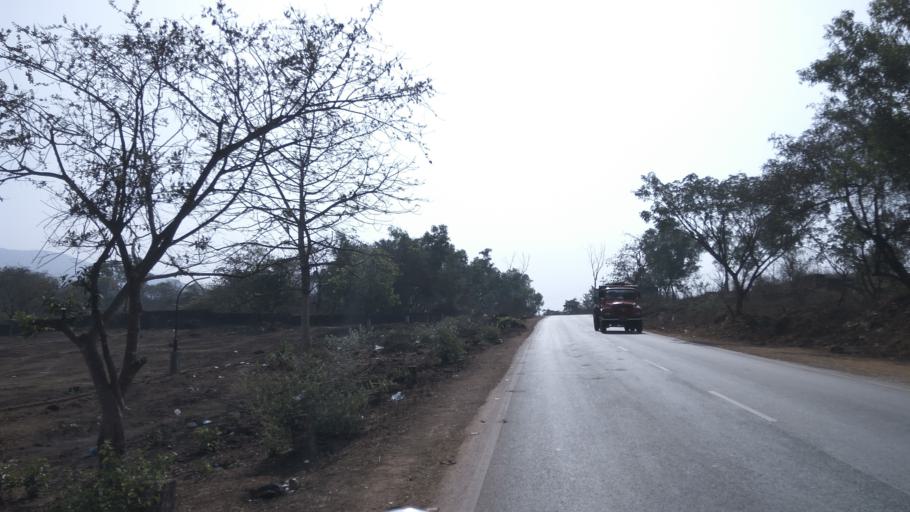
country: IN
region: Goa
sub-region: North Goa
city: Palle
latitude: 15.4162
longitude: 74.0756
